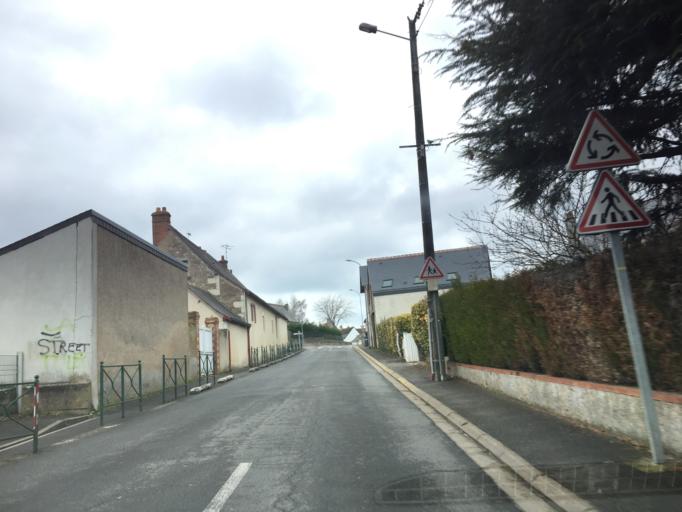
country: FR
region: Centre
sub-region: Departement d'Indre-et-Loire
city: Chanceaux-sur-Choisille
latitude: 47.4724
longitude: 0.7040
